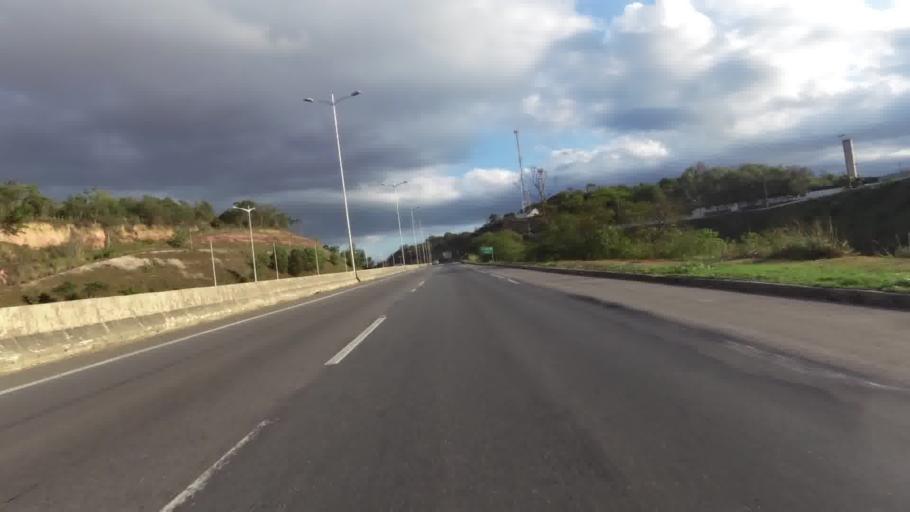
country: BR
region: Espirito Santo
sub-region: Vitoria
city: Vitoria
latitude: -20.2321
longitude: -40.3680
